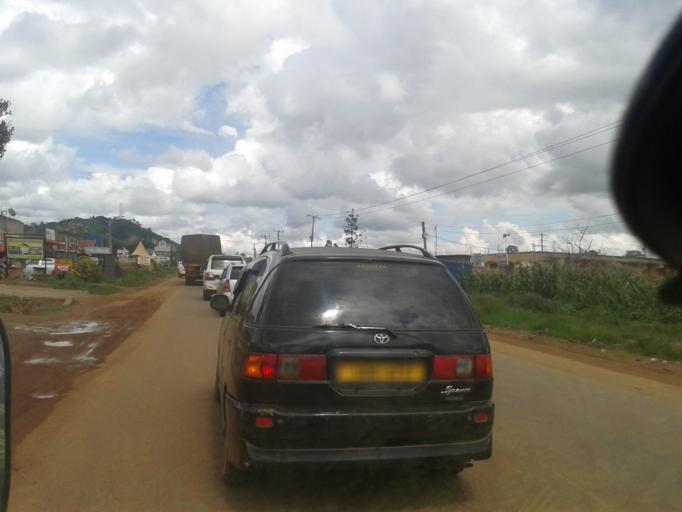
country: UG
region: Central Region
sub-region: Mukono District
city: Mukono
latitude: 0.3661
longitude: 32.8163
